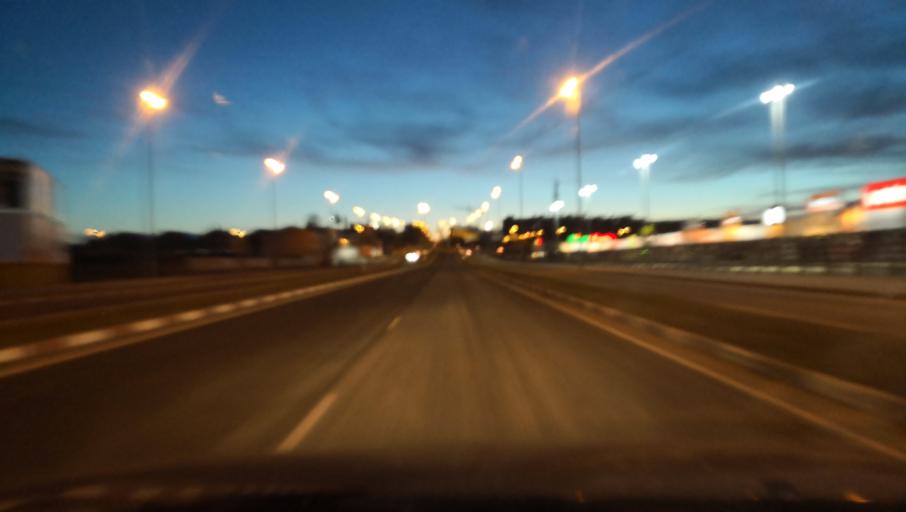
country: ES
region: Castille and Leon
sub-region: Provincia de Zamora
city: Zamora
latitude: 41.5209
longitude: -5.7212
